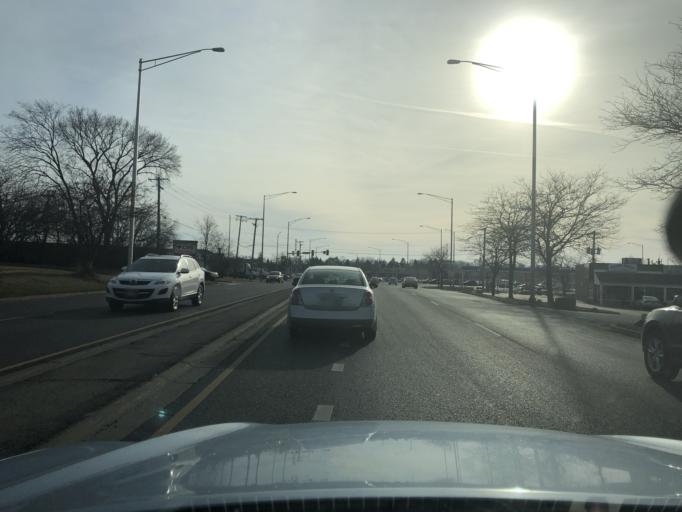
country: US
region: Illinois
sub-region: DuPage County
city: Glendale Heights
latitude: 41.9043
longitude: -88.0816
